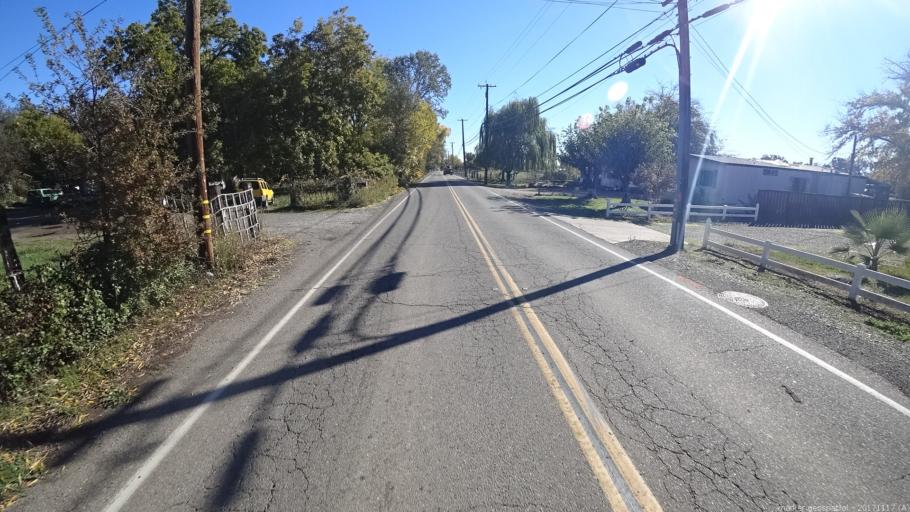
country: US
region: California
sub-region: Shasta County
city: Anderson
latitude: 40.4475
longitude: -122.2555
